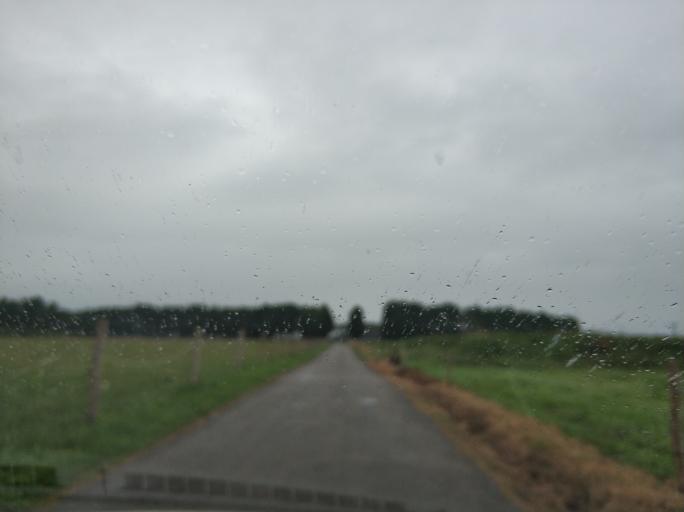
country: ES
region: Asturias
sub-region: Province of Asturias
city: Tineo
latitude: 43.5615
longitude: -6.4681
